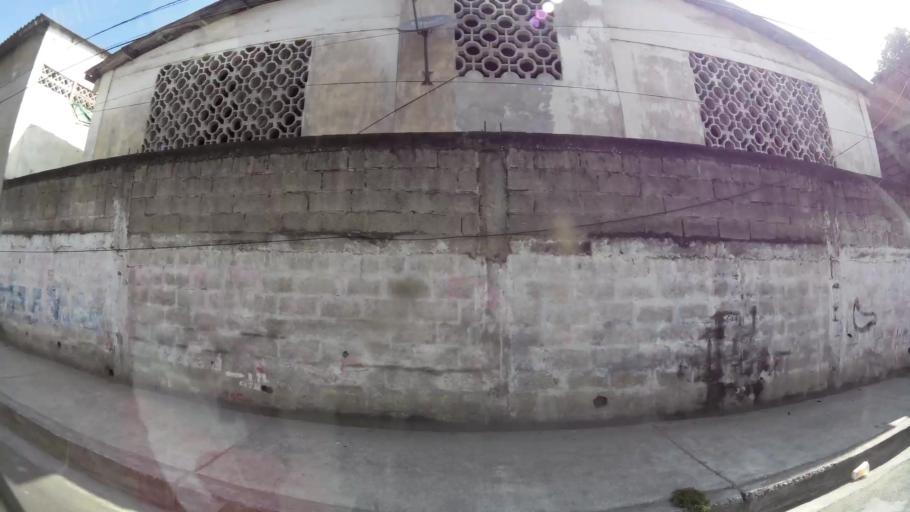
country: EC
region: Guayas
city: Guayaquil
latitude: -2.1541
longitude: -79.9334
